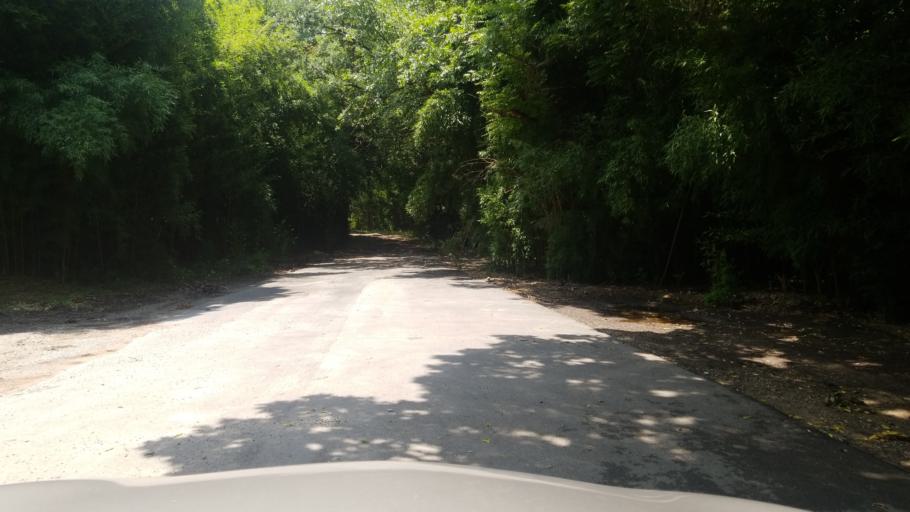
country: US
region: Texas
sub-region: Dallas County
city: Duncanville
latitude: 32.6767
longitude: -96.9214
